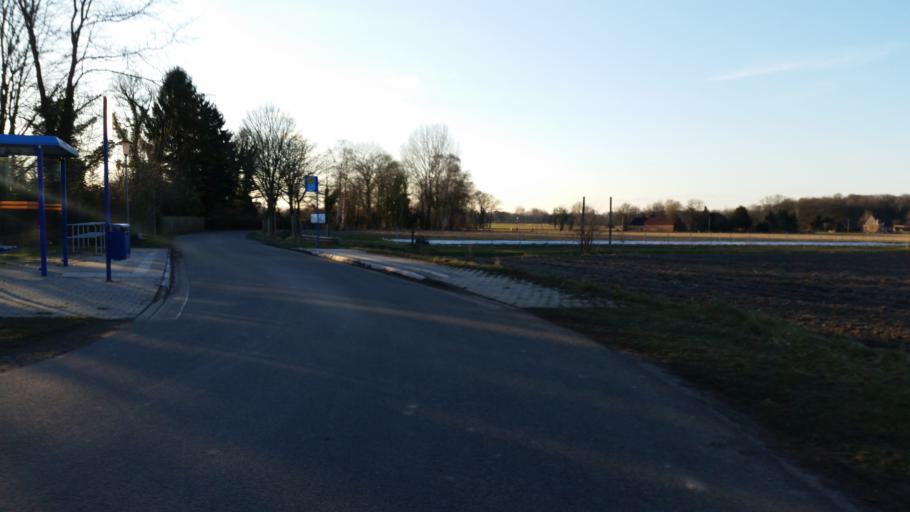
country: DE
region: North Rhine-Westphalia
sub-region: Regierungsbezirk Munster
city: Neuenkirchen
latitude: 52.2734
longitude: 7.3979
